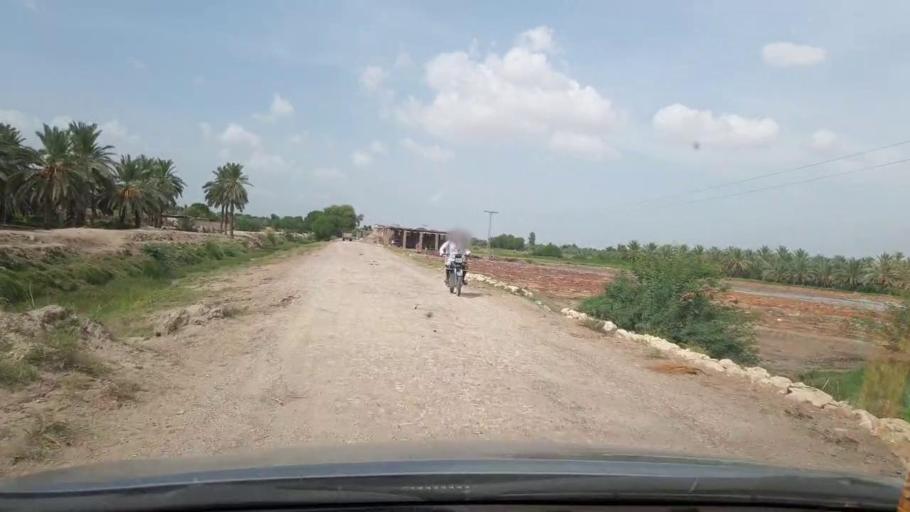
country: PK
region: Sindh
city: Khairpur
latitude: 27.5235
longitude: 68.8848
